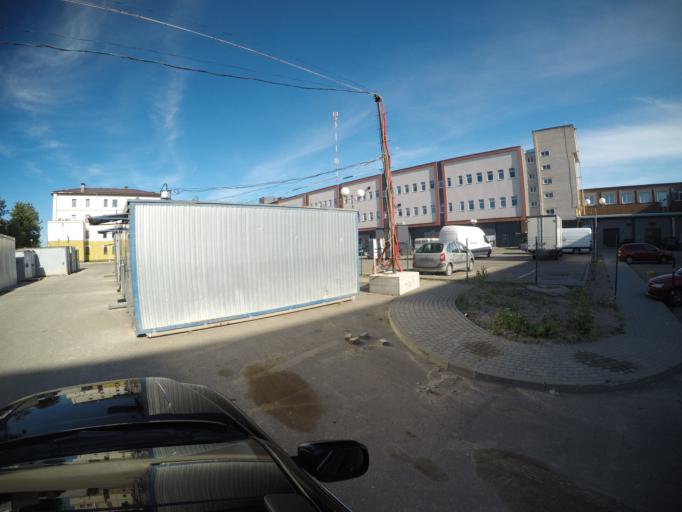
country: BY
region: Grodnenskaya
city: Hrodna
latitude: 53.7110
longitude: 23.8244
